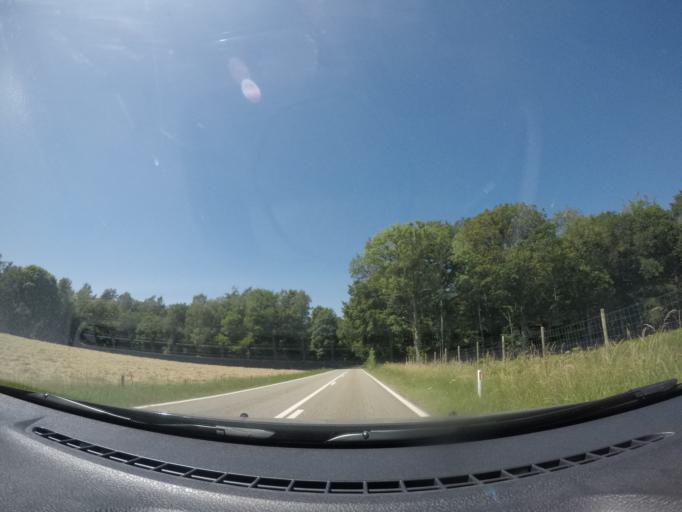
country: BE
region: Wallonia
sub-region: Province du Luxembourg
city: Daverdisse
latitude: 50.0232
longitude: 5.1605
